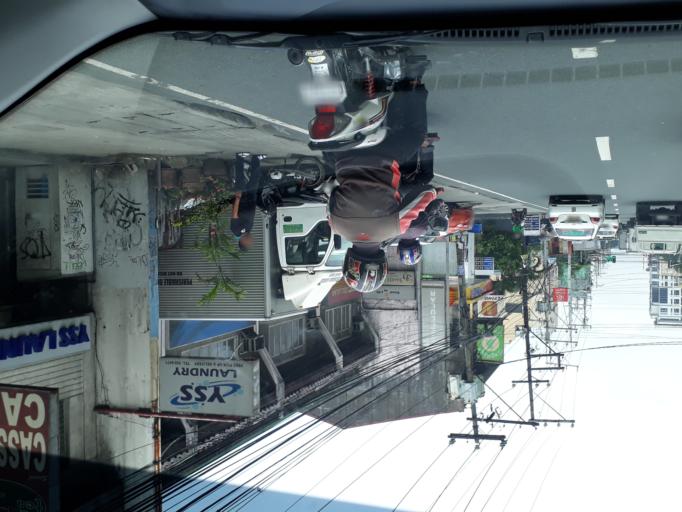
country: PH
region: Calabarzon
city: Del Monte
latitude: 14.6180
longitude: 121.0066
